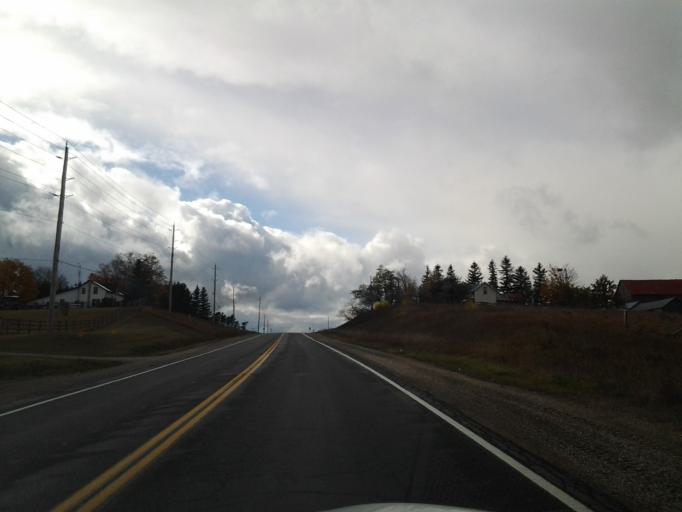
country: CA
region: Ontario
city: Shelburne
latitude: 44.1028
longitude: -80.0828
